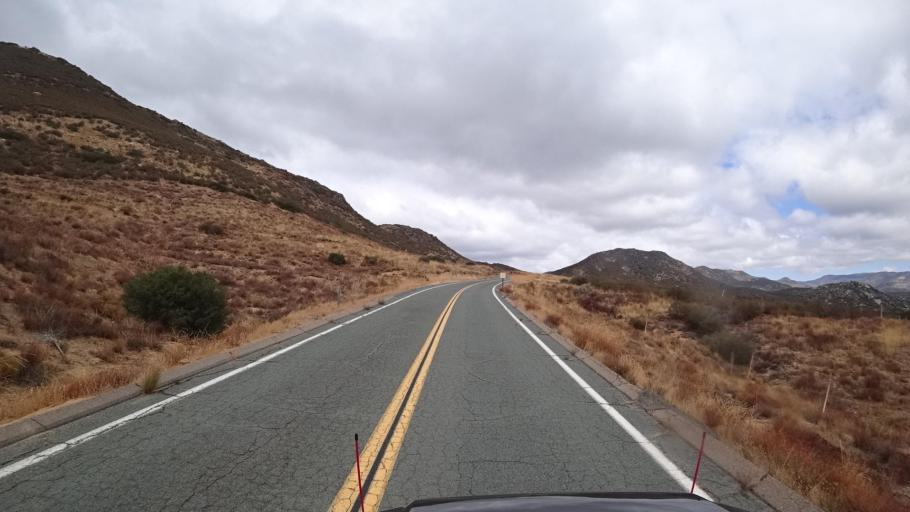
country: US
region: California
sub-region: San Diego County
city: Pine Valley
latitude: 32.7372
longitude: -116.4535
